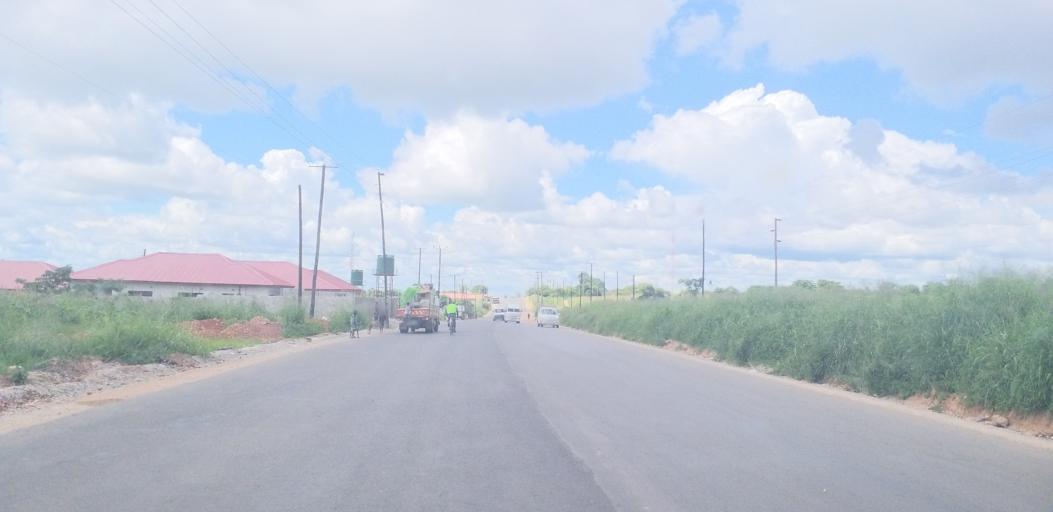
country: ZM
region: Lusaka
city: Lusaka
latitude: -15.3545
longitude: 28.3241
